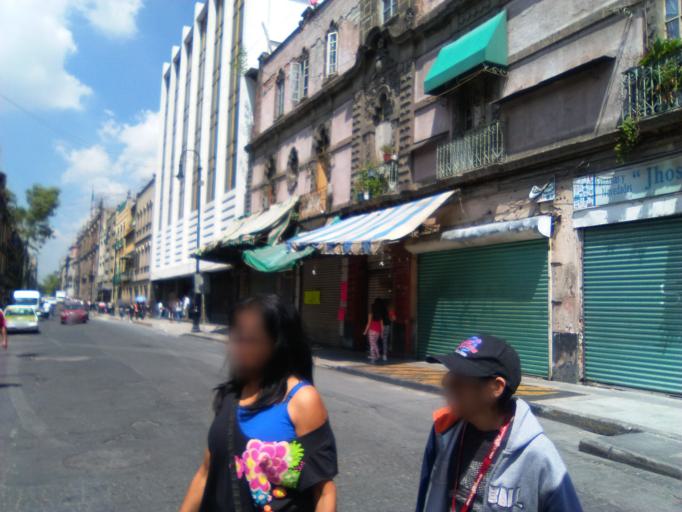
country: MX
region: Mexico City
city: Mexico City
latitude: 19.4352
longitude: -99.1298
